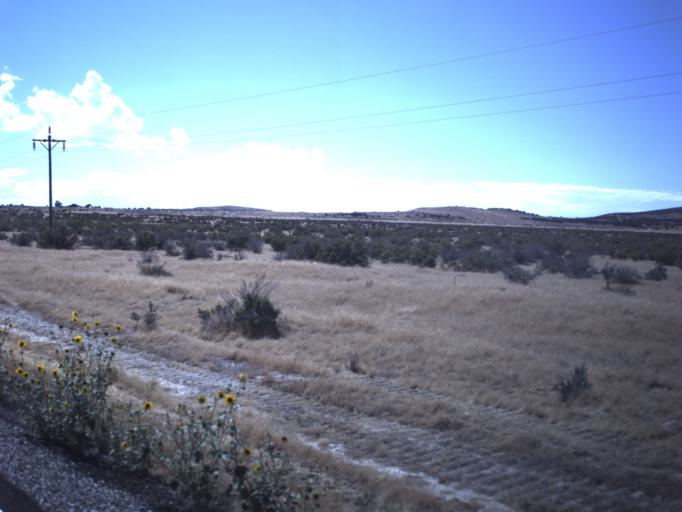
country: US
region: Utah
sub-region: Tooele County
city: Grantsville
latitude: 40.2420
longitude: -112.7125
